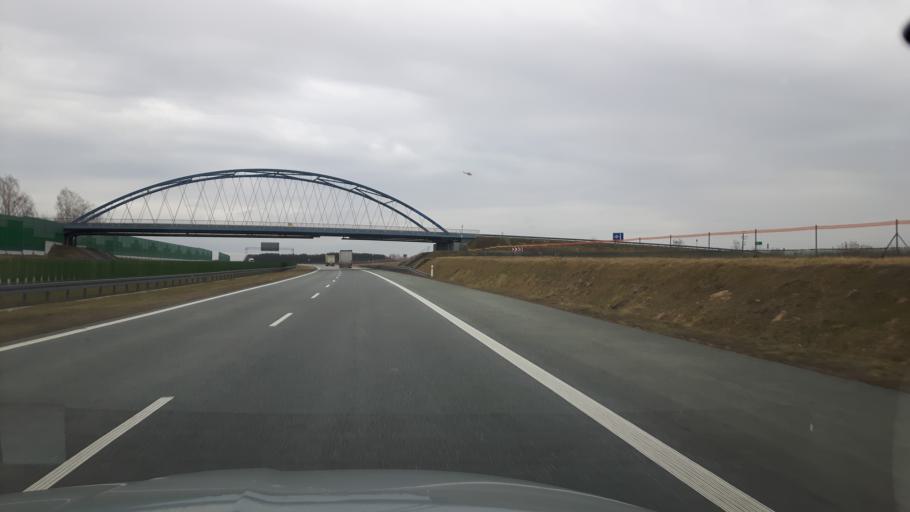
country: PL
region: Masovian Voivodeship
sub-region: Powiat minski
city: Jakubow
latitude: 52.2058
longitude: 21.6735
